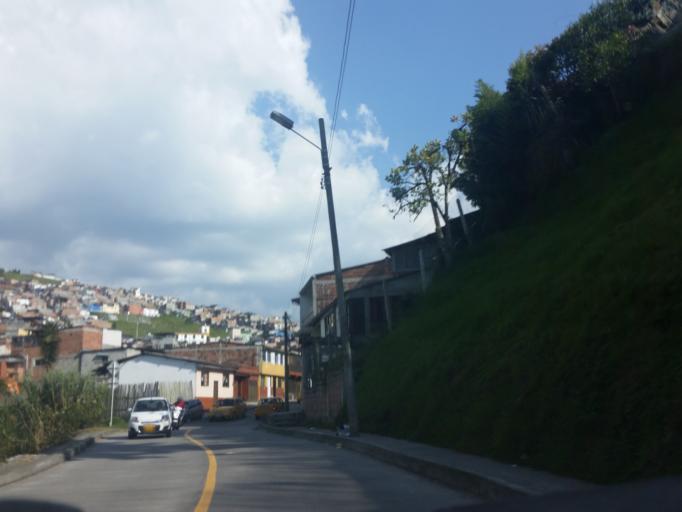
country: CO
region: Caldas
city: Manizales
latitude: 5.0699
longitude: -75.4952
